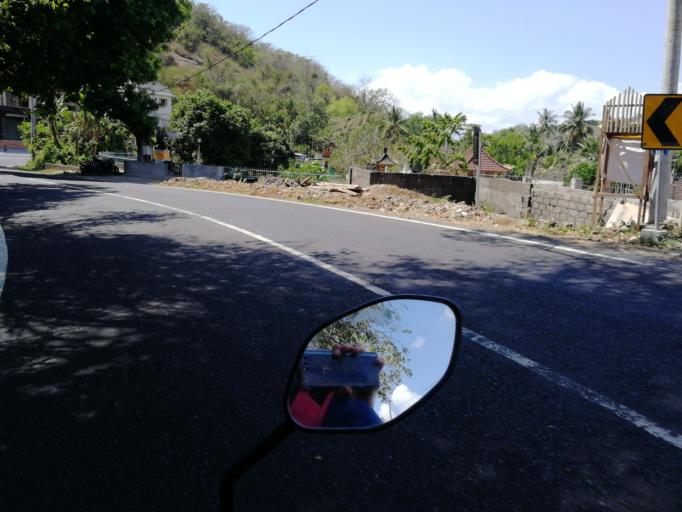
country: ID
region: Bali
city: Padangbai
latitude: -8.5251
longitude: 115.5039
